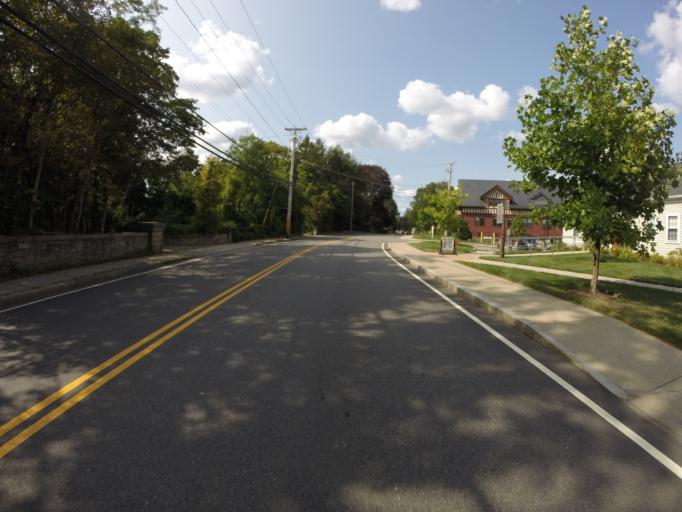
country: US
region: Massachusetts
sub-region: Bristol County
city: Easton
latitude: 42.0686
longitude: -71.1052
